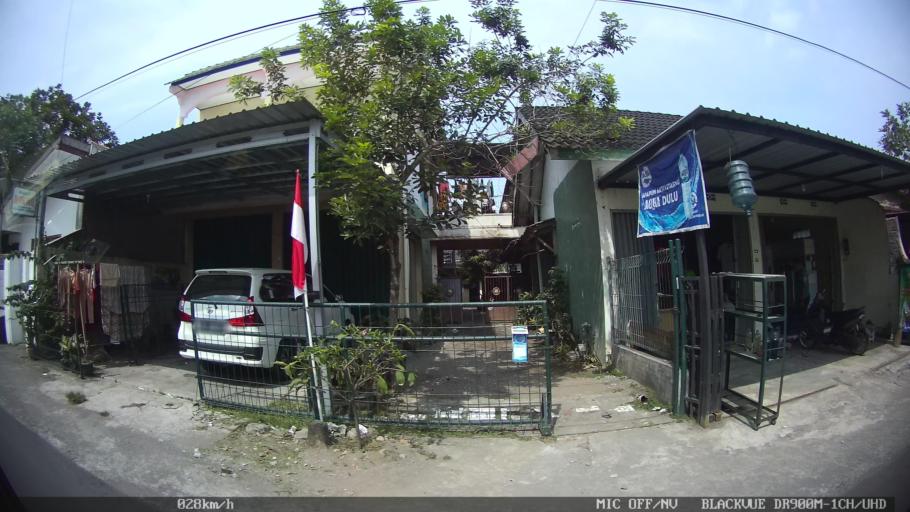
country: ID
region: Daerah Istimewa Yogyakarta
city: Depok
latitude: -7.7868
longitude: 110.4058
